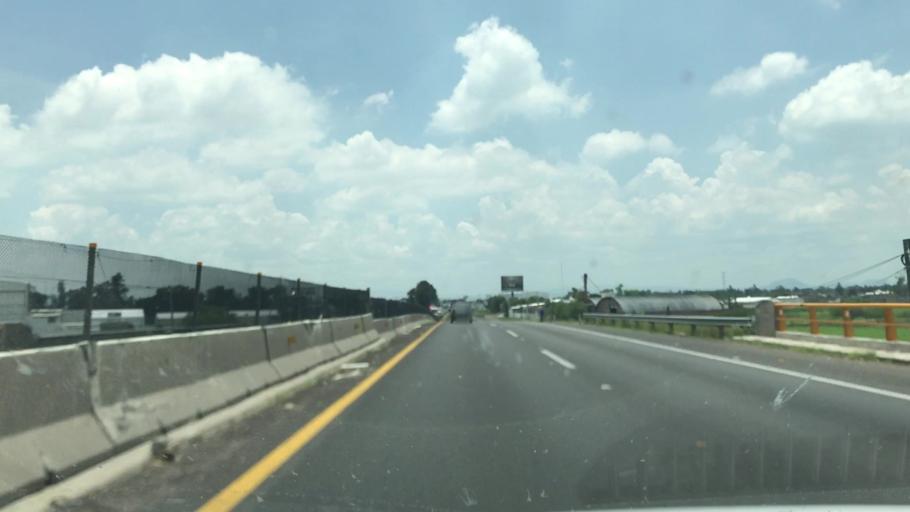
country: MX
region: Guanajuato
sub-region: Irapuato
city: San Jose de Bernalejo (El Guayabo)
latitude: 20.6124
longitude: -101.4069
